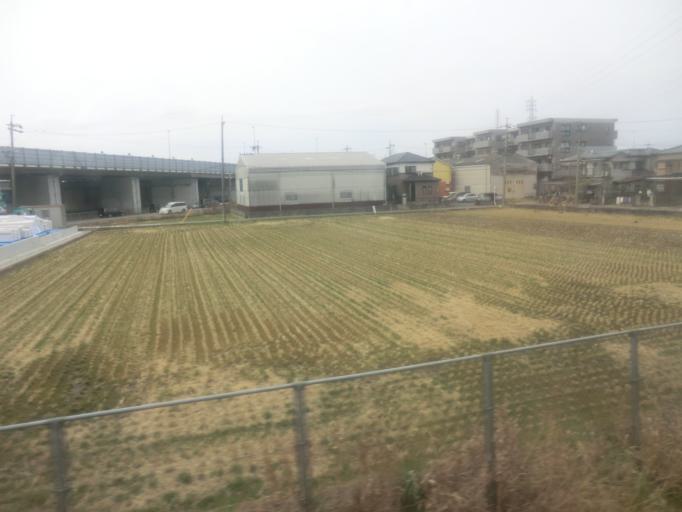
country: JP
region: Aichi
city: Ichinomiya
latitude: 35.2779
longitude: 136.8086
